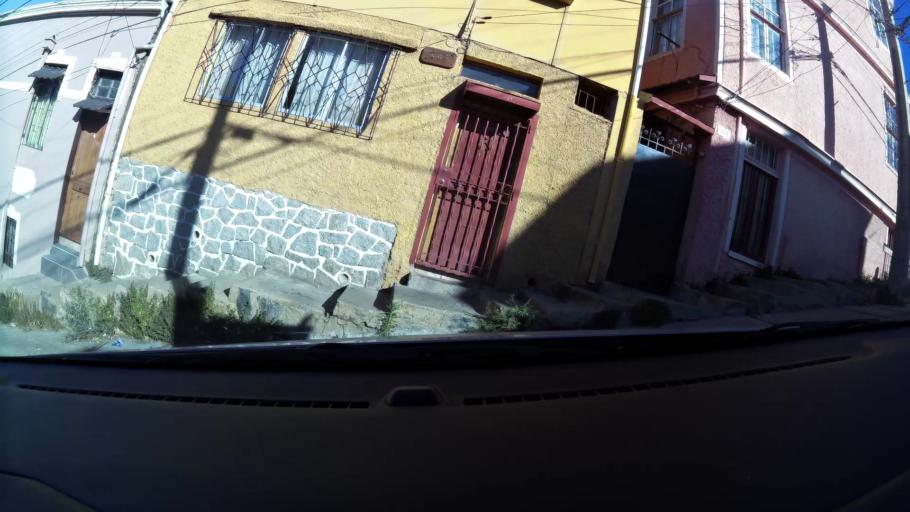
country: CL
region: Valparaiso
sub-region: Provincia de Valparaiso
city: Valparaiso
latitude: -33.0527
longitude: -71.6159
